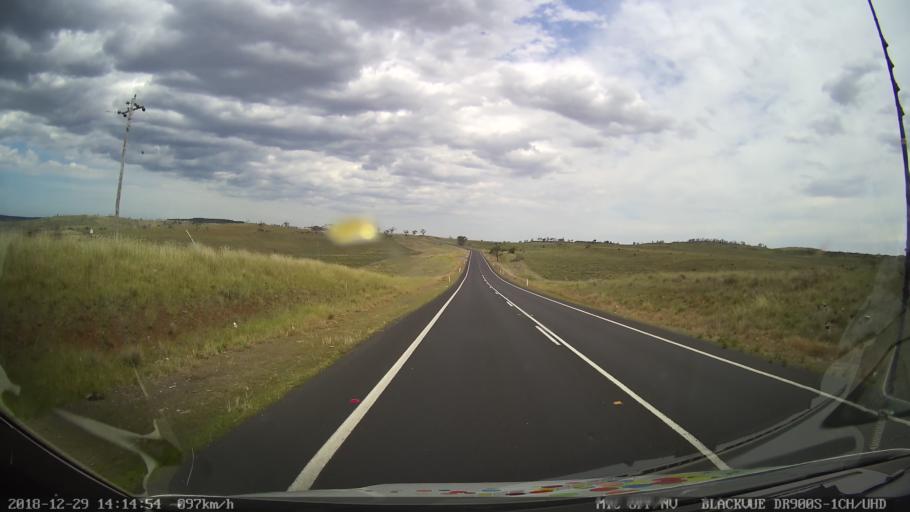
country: AU
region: New South Wales
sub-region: Cooma-Monaro
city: Cooma
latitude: -36.4486
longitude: 149.2369
